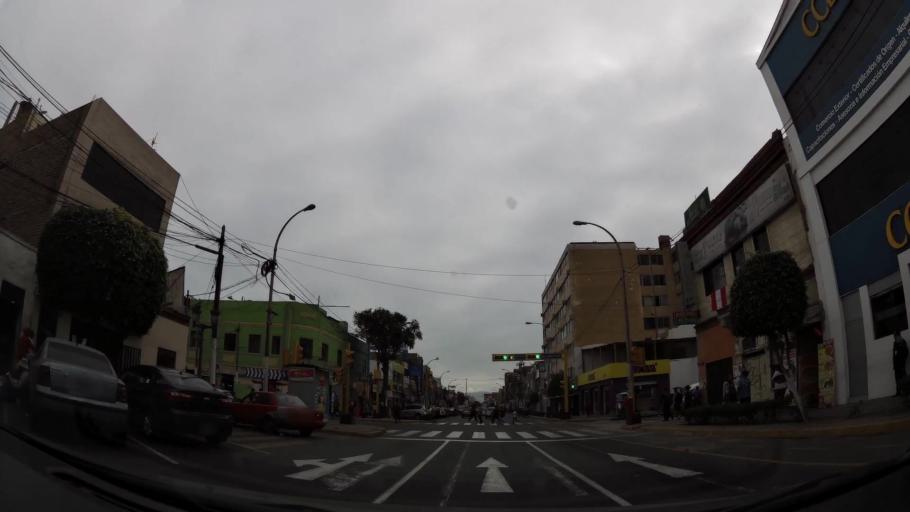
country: PE
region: Callao
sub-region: Callao
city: Callao
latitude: -12.0600
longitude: -77.1368
